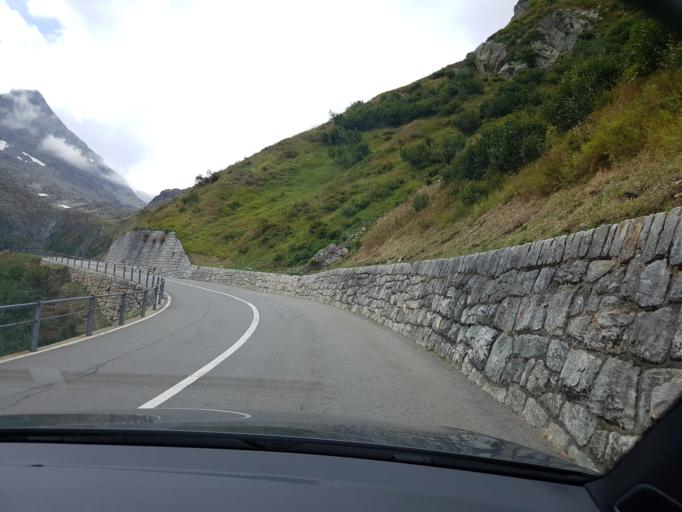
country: CH
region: Obwalden
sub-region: Obwalden
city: Engelberg
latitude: 46.7410
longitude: 8.4609
